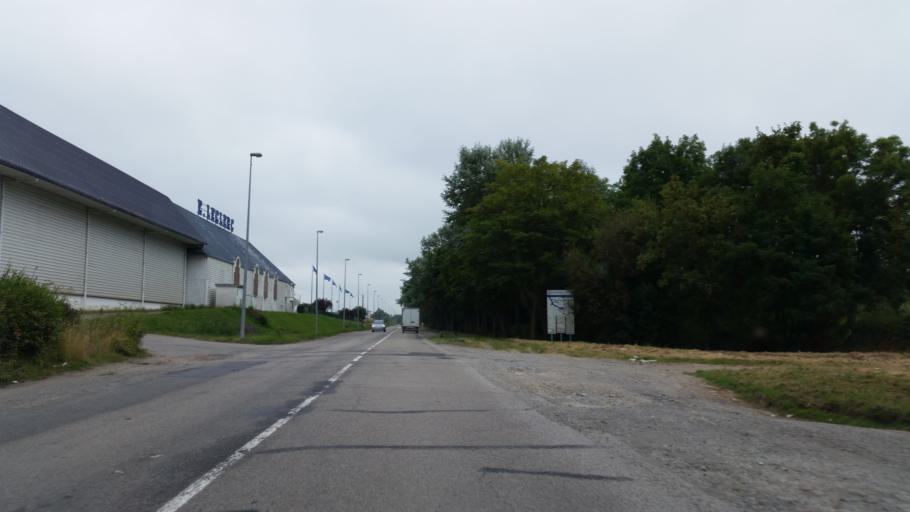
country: FR
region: Lower Normandy
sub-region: Departement du Calvados
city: La Riviere-Saint-Sauveur
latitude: 49.4136
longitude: 0.2591
